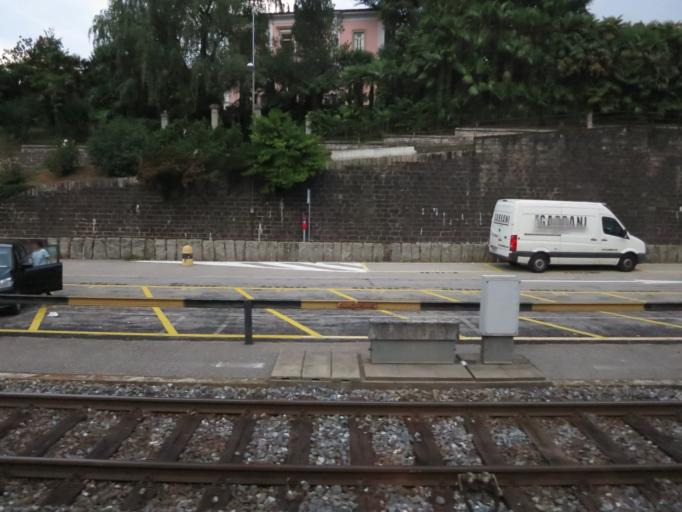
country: CH
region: Ticino
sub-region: Lugano District
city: Sorengo
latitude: 46.0038
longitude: 8.9472
